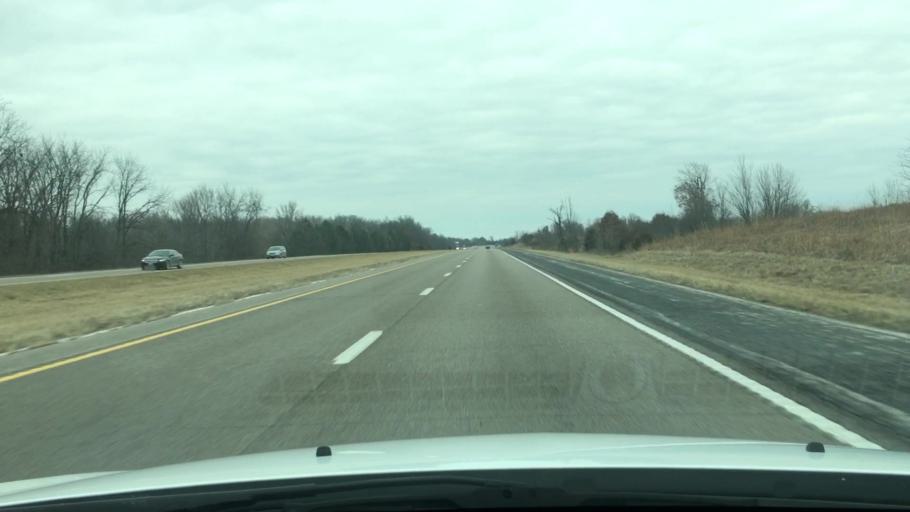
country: US
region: Missouri
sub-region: Callaway County
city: Fulton
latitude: 38.9907
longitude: -91.8936
